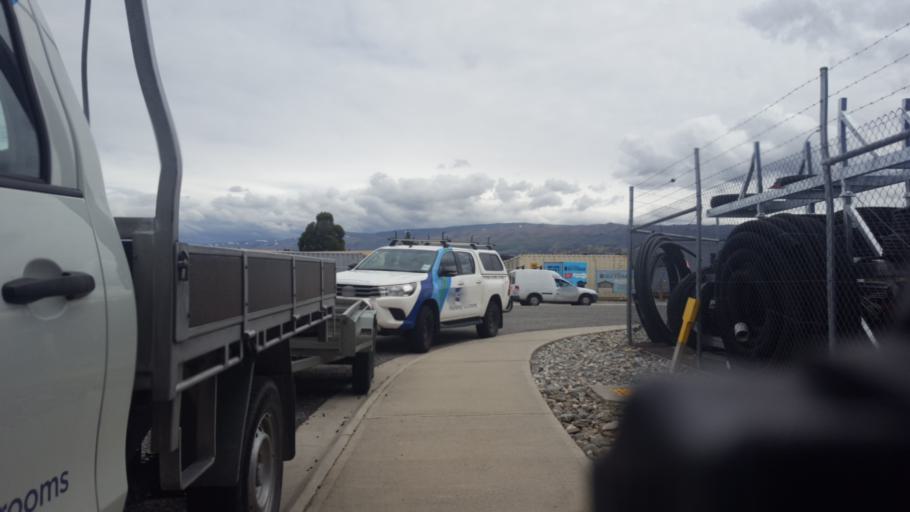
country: NZ
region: Otago
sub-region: Queenstown-Lakes District
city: Wanaka
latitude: -45.2474
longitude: 169.3715
